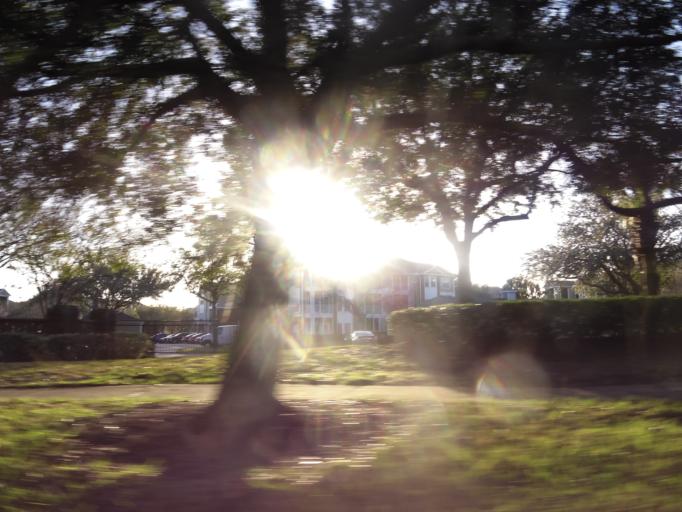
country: US
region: Florida
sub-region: Duval County
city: Jacksonville
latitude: 30.2667
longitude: -81.5506
